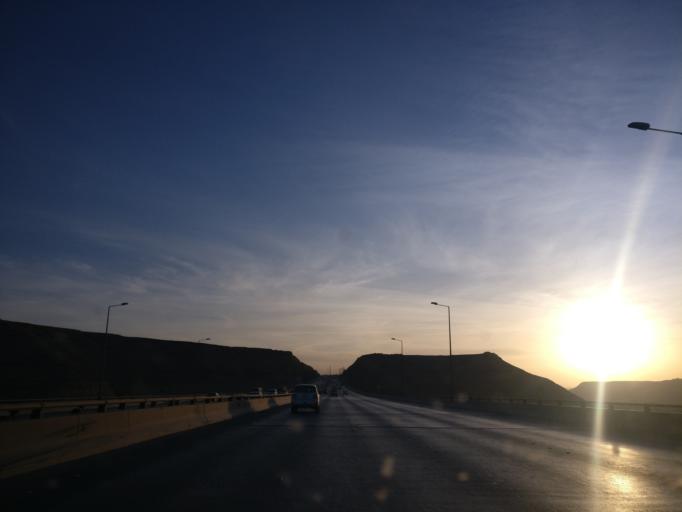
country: SA
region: Ar Riyad
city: Riyadh
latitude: 24.6141
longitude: 46.5673
